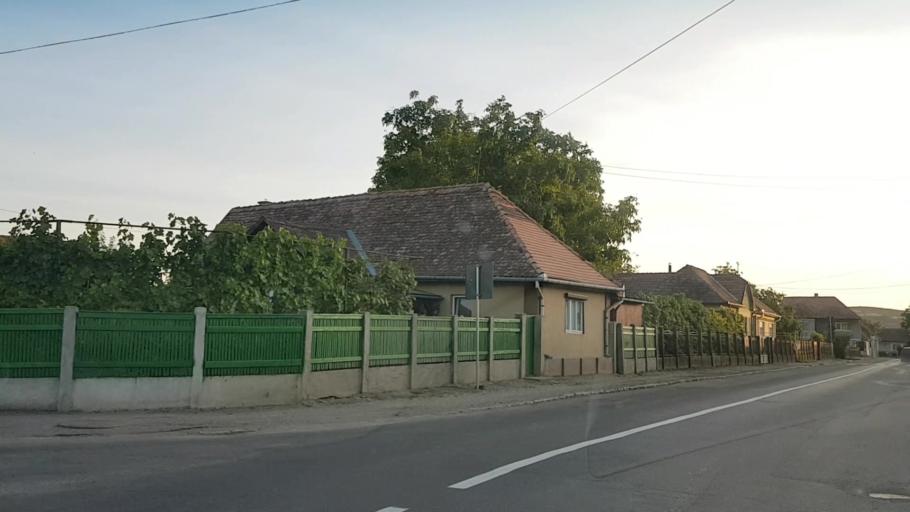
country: RO
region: Harghita
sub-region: Oras Cristuru Secuiesc
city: Cristuru Secuiesc
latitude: 46.2844
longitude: 25.0281
